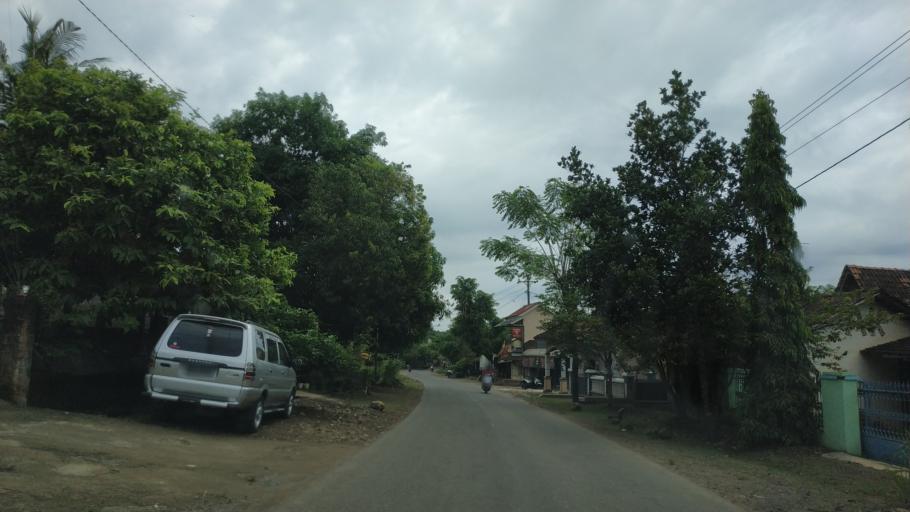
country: ID
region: Central Java
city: Krajan Tegalombo
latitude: -6.4435
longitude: 110.9837
